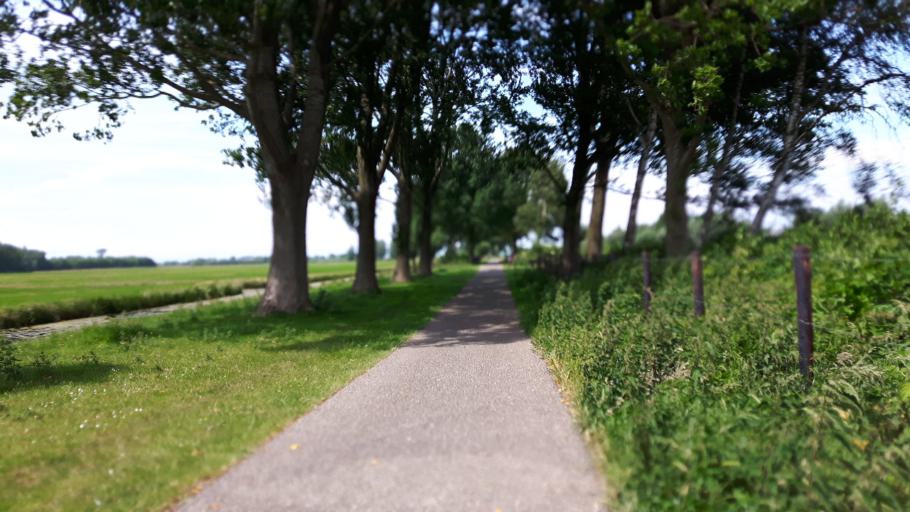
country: NL
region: North Holland
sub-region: Gemeente Aalsmeer
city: Aalsmeer
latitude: 52.2018
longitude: 4.7360
